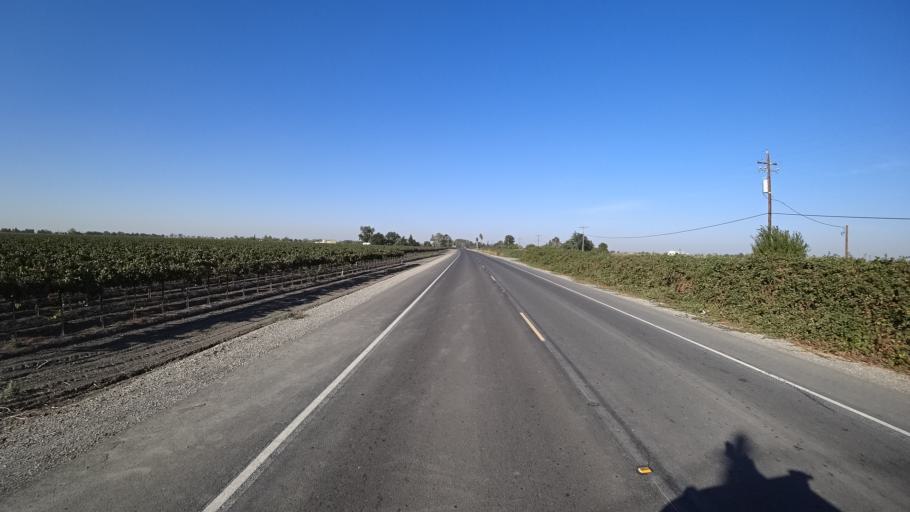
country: US
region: California
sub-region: Sacramento County
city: Parkway
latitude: 38.4145
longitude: -121.5735
